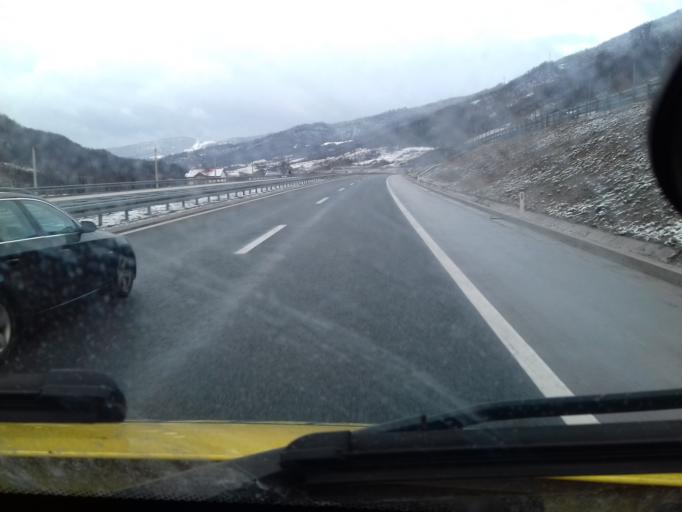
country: BA
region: Federation of Bosnia and Herzegovina
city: Kakanj
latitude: 44.1333
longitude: 18.0549
